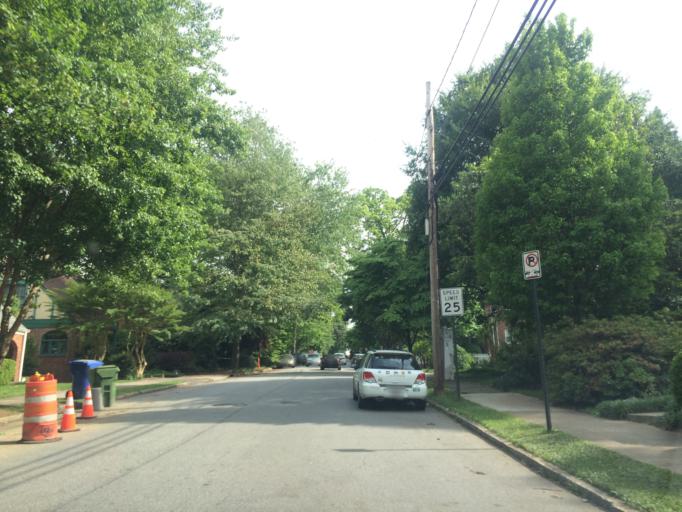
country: US
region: Georgia
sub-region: DeKalb County
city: Druid Hills
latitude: 33.7779
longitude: -84.3587
